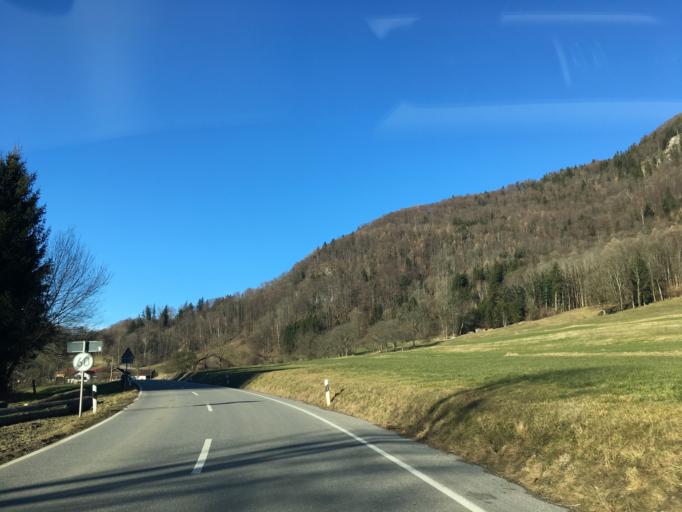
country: DE
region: Bavaria
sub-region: Upper Bavaria
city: Nussdorf am Inn
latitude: 47.7181
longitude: 12.1652
